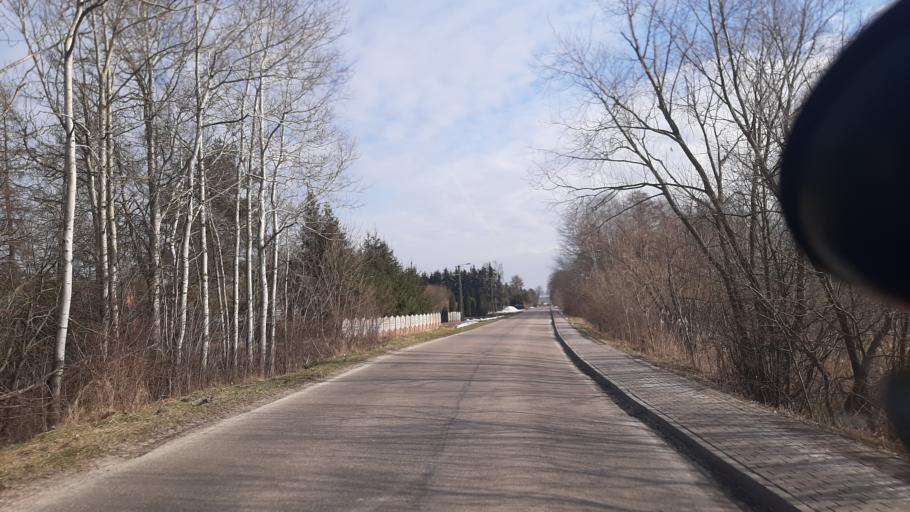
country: PL
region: Lublin Voivodeship
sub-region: Powiat lubartowski
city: Uscimow Stary
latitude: 51.4716
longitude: 22.9467
